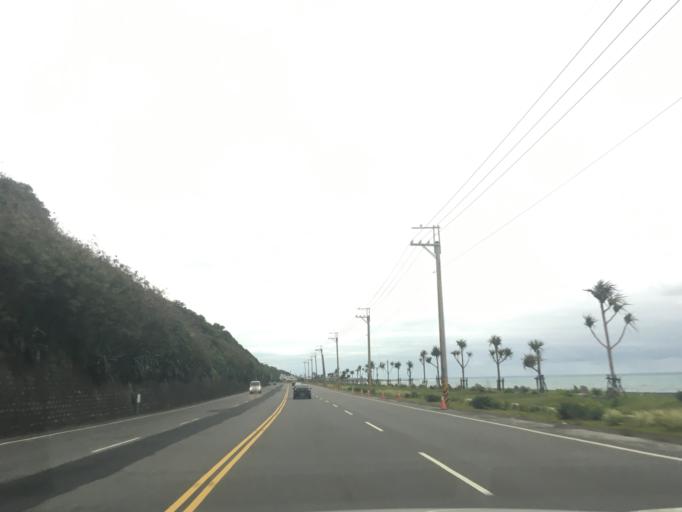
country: TW
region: Taiwan
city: Hengchun
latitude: 22.3453
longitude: 120.8987
